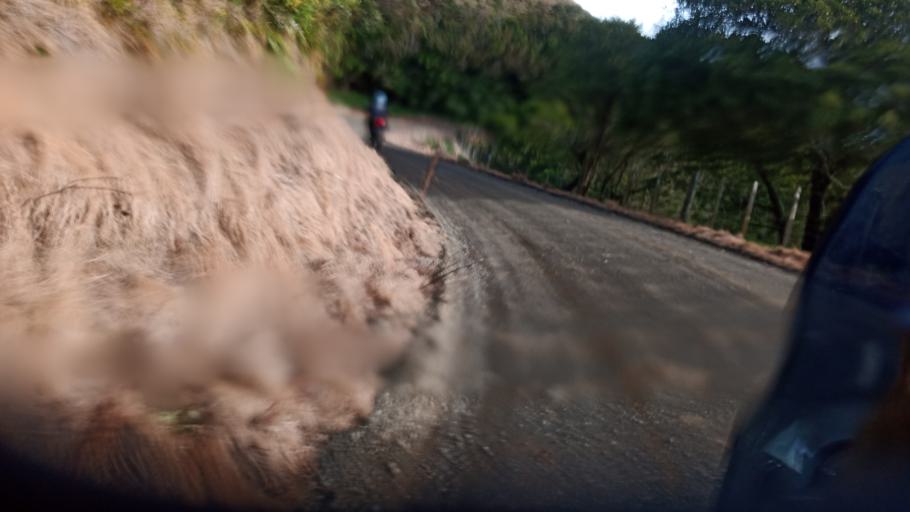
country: NZ
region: Gisborne
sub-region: Gisborne District
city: Gisborne
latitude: -38.4620
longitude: 177.5378
